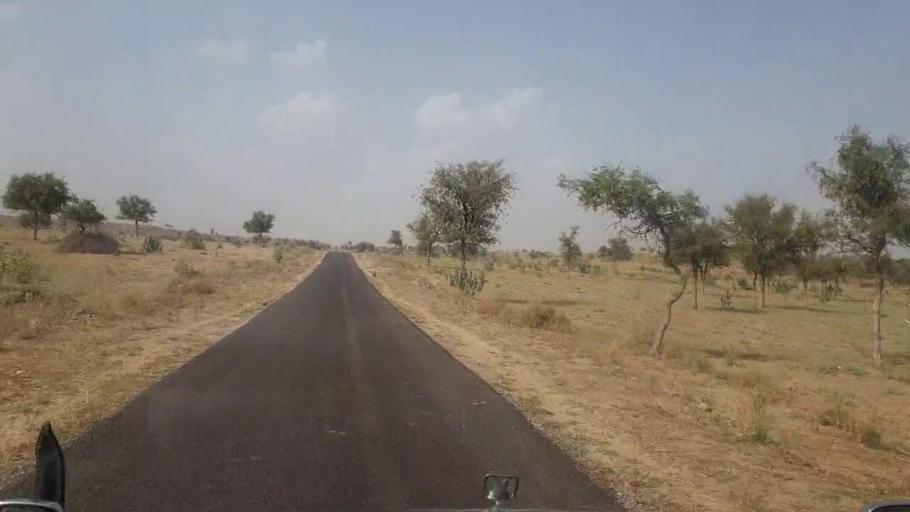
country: PK
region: Sindh
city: Islamkot
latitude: 25.1848
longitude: 70.2865
